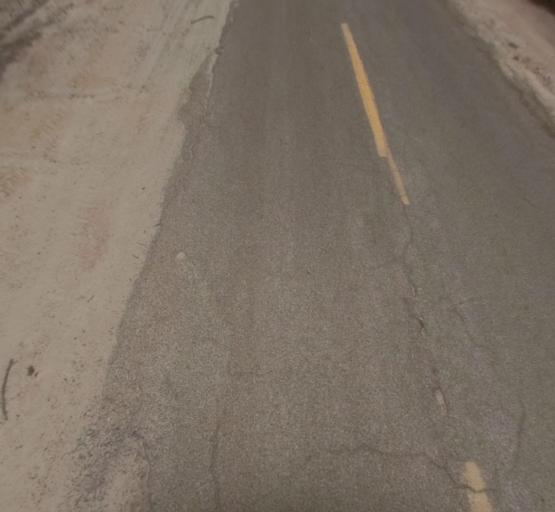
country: US
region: California
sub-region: Fresno County
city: Kerman
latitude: 36.8149
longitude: -120.1701
